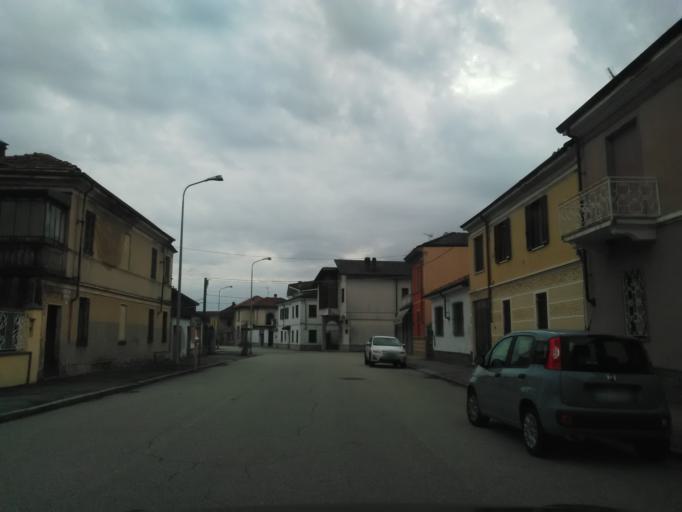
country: IT
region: Piedmont
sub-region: Provincia di Vercelli
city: San Germano Vercellese
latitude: 45.3520
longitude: 8.2471
